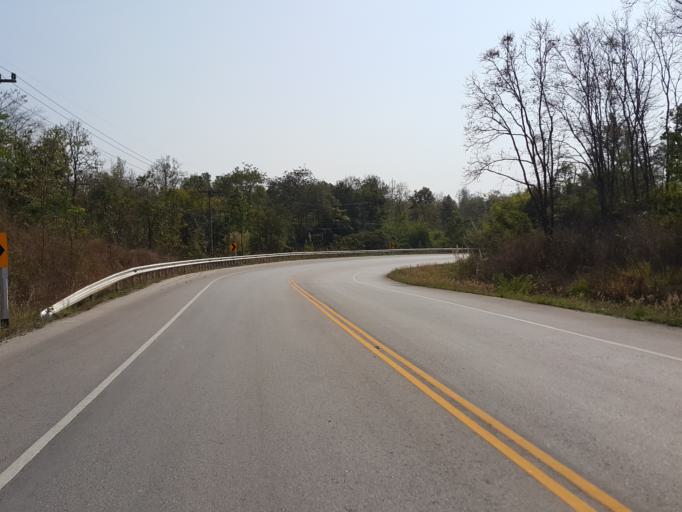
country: TH
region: Lampang
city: Wang Nuea
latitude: 18.9473
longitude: 99.6121
